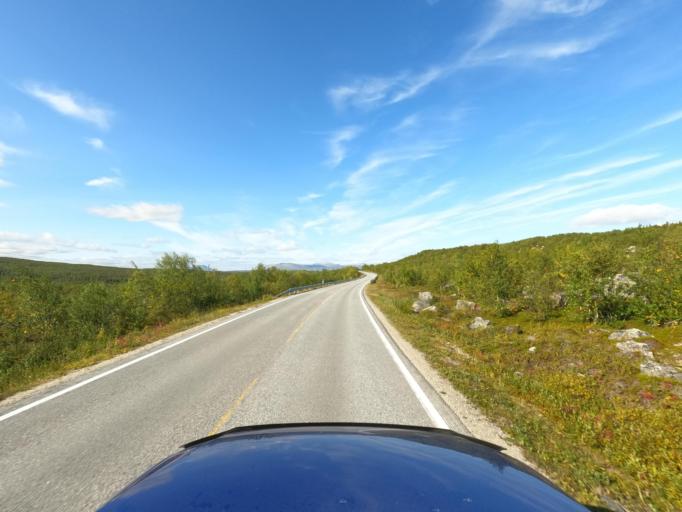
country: NO
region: Finnmark Fylke
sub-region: Porsanger
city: Lakselv
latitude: 69.7654
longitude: 25.1789
